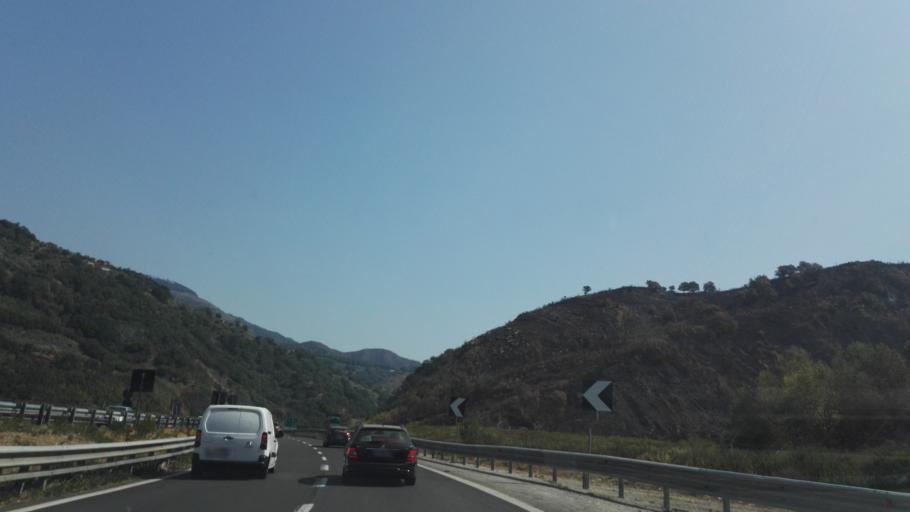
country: IT
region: Calabria
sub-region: Provincia di Catanzaro
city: San Mango d'Aquino
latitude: 39.0732
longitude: 16.1897
